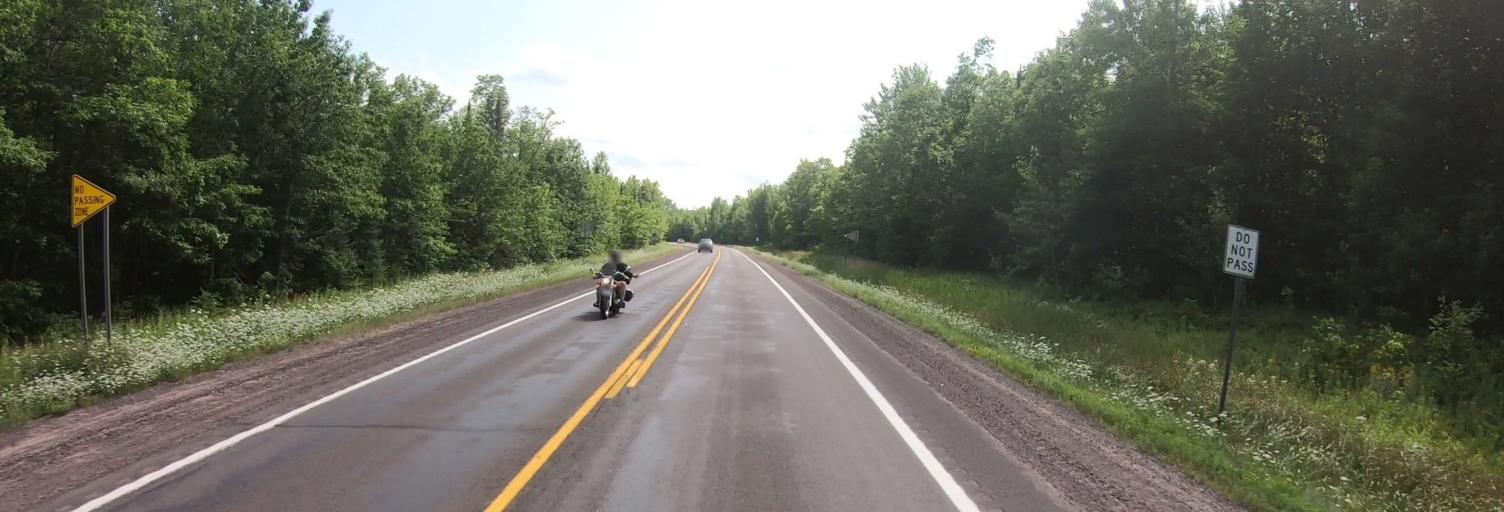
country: US
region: Michigan
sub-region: Ontonagon County
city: Ontonagon
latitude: 46.8303
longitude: -88.9965
